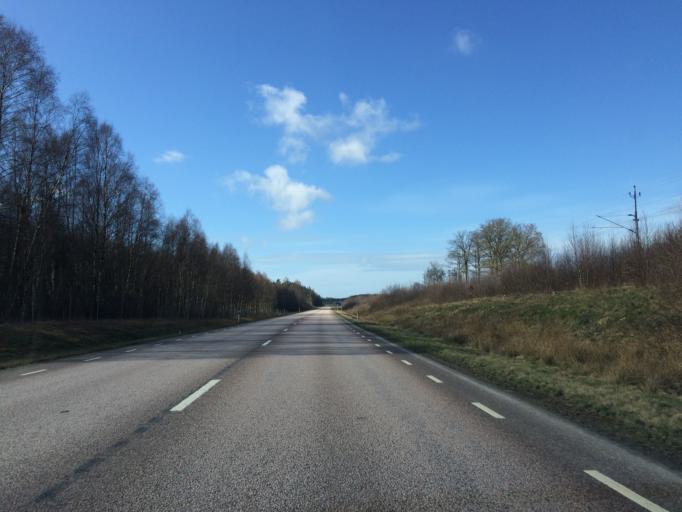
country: SE
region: Halland
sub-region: Laholms Kommun
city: Knared
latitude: 56.5181
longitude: 13.2913
